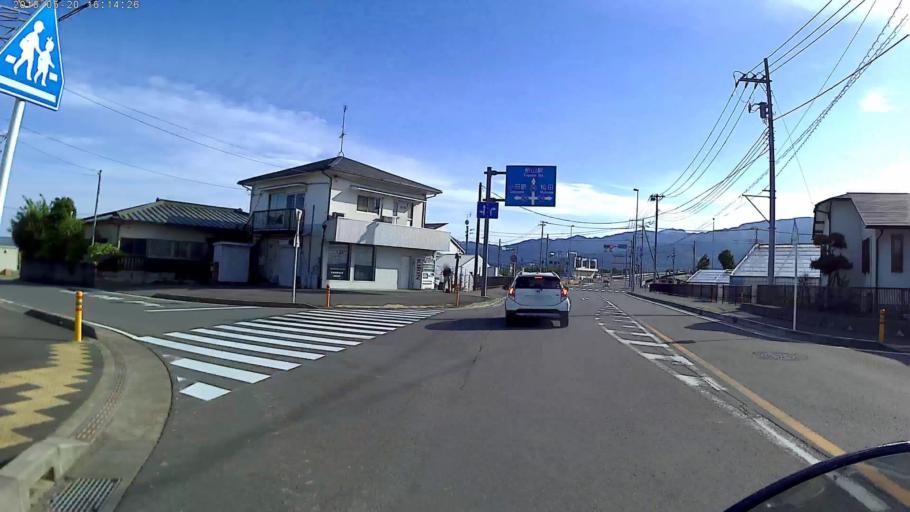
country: JP
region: Kanagawa
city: Odawara
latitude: 35.3144
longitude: 139.1538
